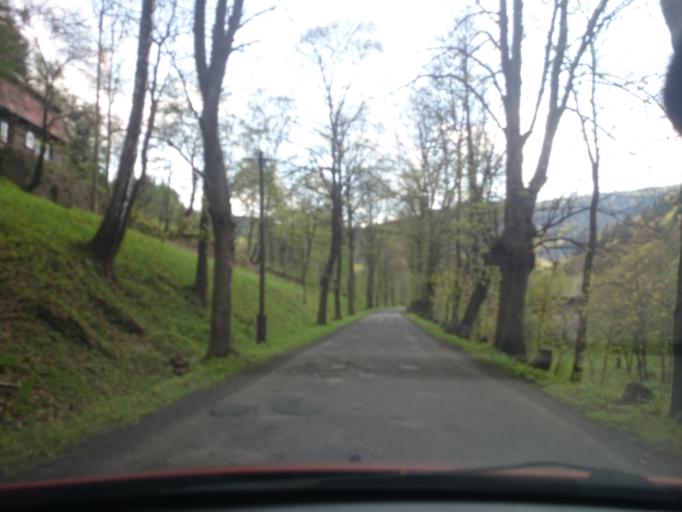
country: PL
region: Lower Silesian Voivodeship
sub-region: Powiat klodzki
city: Bystrzyca Klodzka
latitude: 50.3004
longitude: 16.5561
